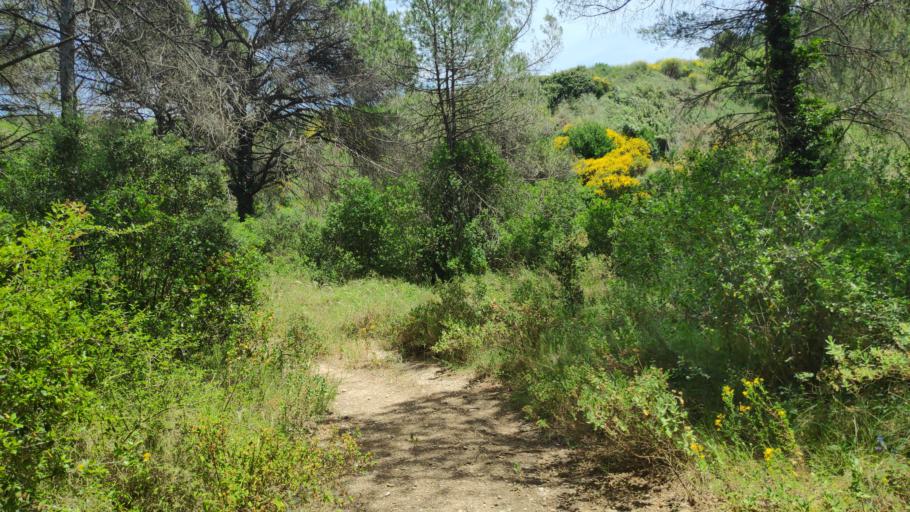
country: ES
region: Catalonia
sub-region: Provincia de Barcelona
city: Rubi
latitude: 41.5007
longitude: 2.0604
